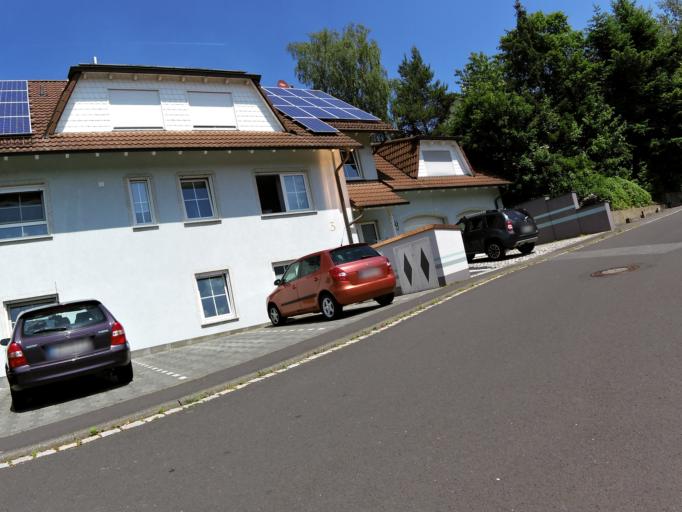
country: DE
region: Bavaria
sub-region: Regierungsbezirk Unterfranken
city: Eisingen
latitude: 49.7615
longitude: 9.8243
